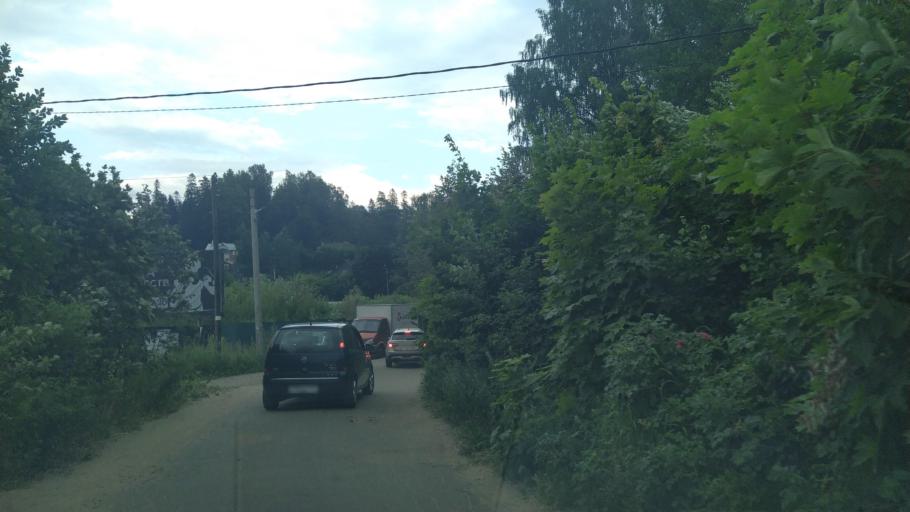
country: RU
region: Leningrad
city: Toksovo
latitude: 60.1739
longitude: 30.5273
